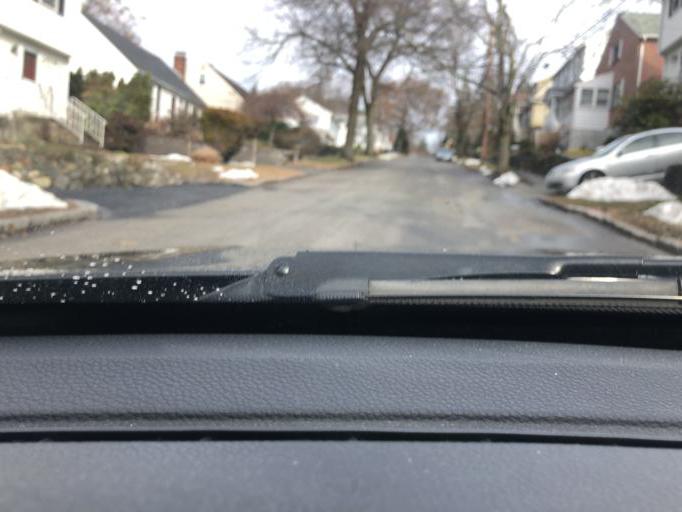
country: US
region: Massachusetts
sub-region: Middlesex County
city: Arlington
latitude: 42.4249
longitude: -71.1646
